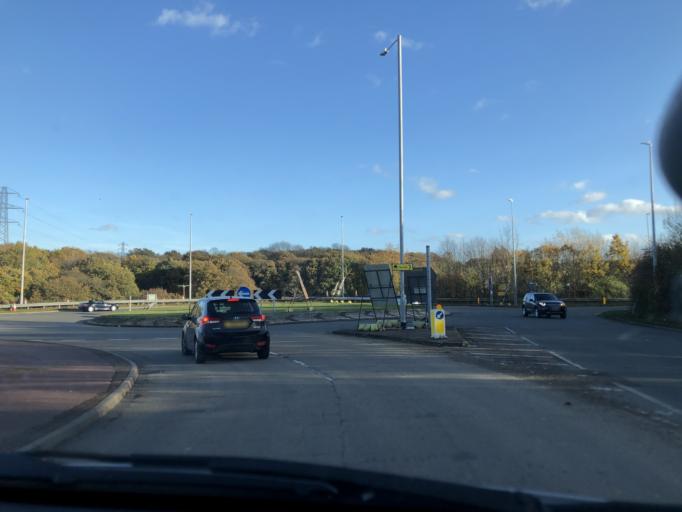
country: GB
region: England
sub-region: Kent
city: Greenhithe
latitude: 51.4301
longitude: 0.2819
